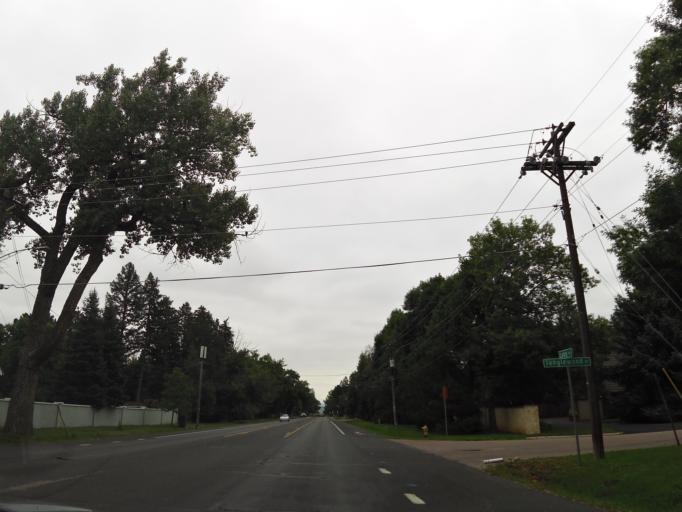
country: US
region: Colorado
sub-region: El Paso County
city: Colorado Springs
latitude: 38.7928
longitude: -104.8422
